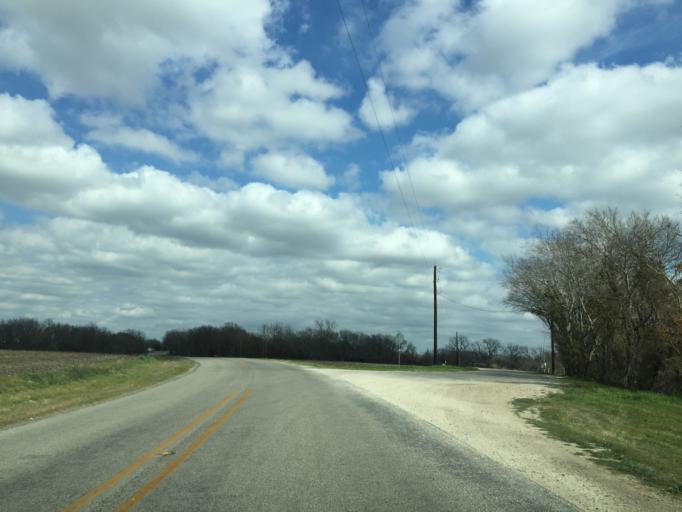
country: US
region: Texas
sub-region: Williamson County
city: Granger
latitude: 30.7088
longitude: -97.4615
